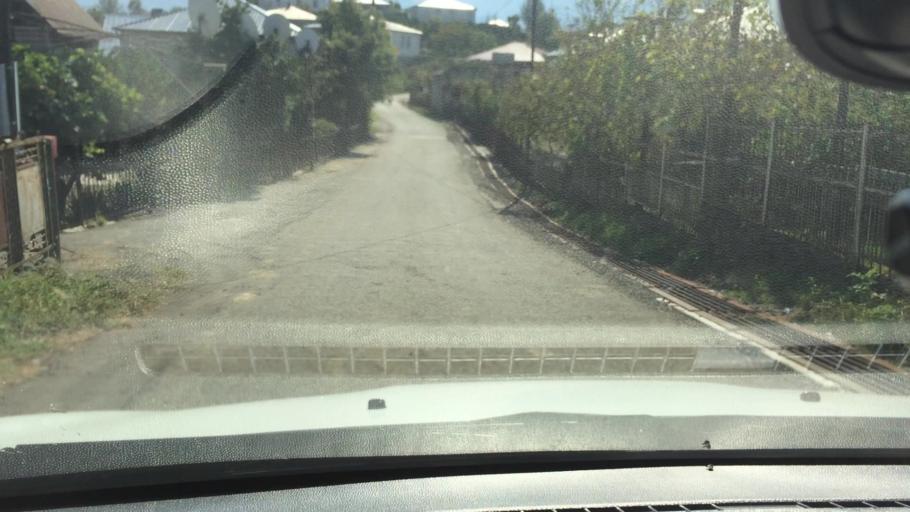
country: GE
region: Ajaria
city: Kobuleti
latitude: 41.8138
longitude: 41.8237
